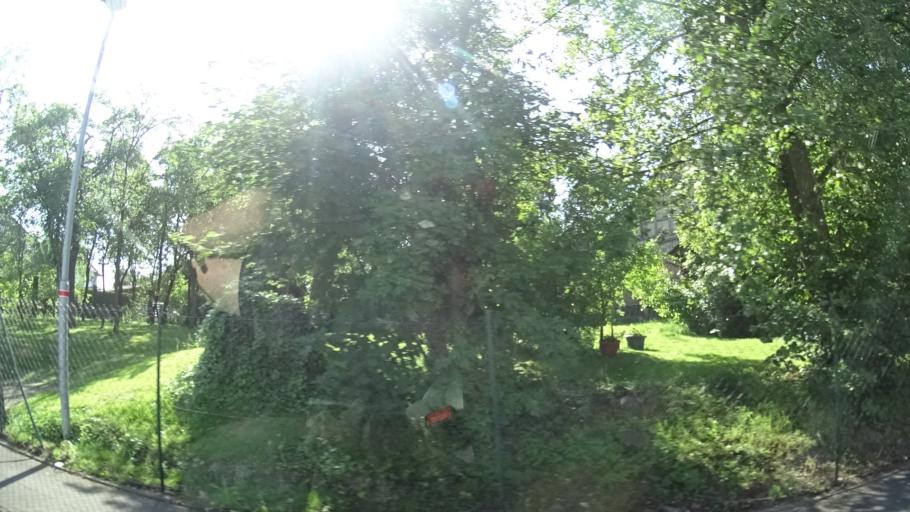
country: DE
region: Hesse
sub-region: Regierungsbezirk Giessen
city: Ebsdorfergrund
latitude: 50.7454
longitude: 8.8347
